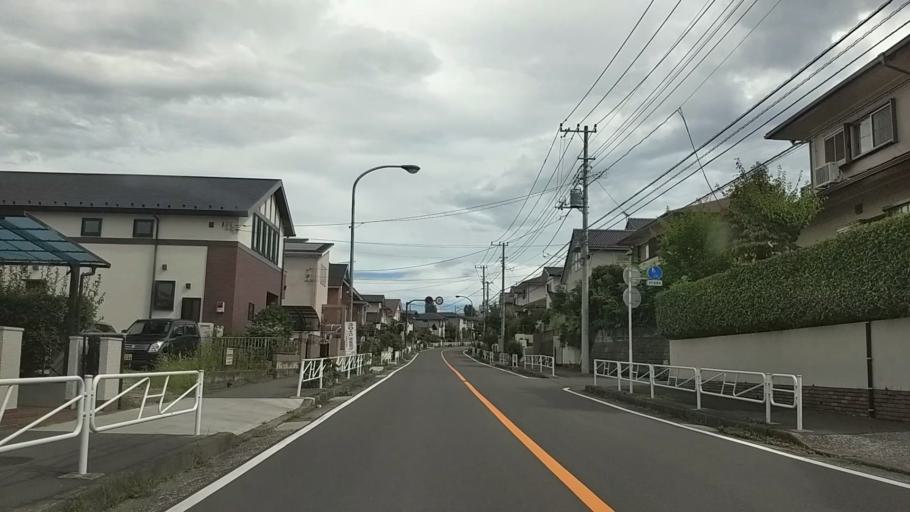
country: JP
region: Tokyo
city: Hachioji
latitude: 35.6344
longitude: 139.3435
